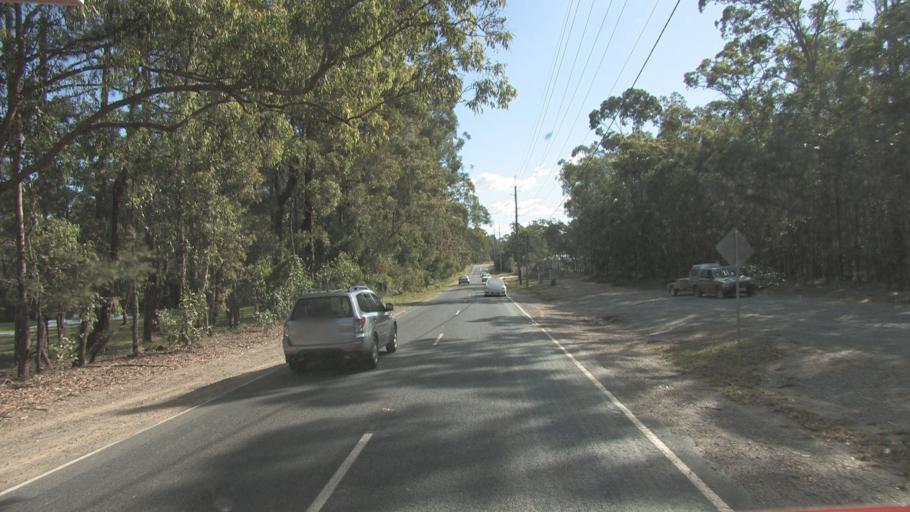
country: AU
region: Queensland
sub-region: Gold Coast
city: Yatala
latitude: -27.6585
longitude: 153.2338
